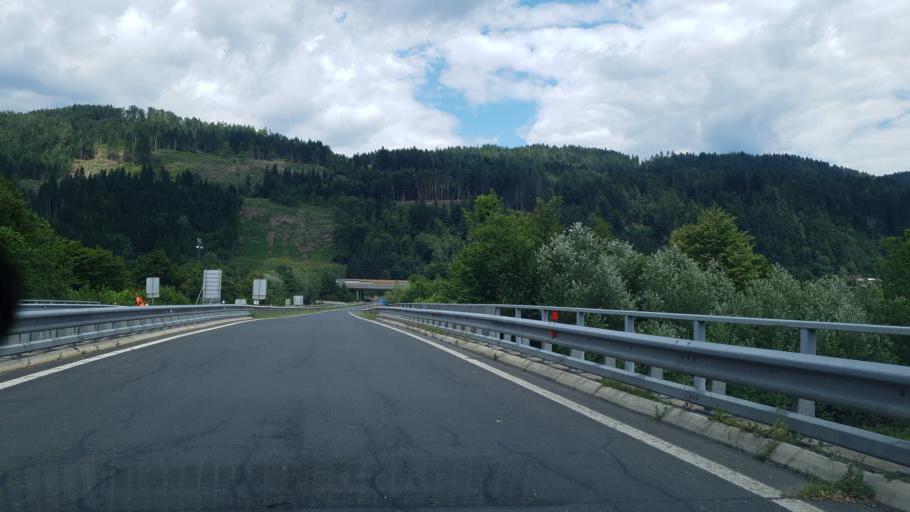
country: AT
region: Carinthia
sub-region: Politischer Bezirk Spittal an der Drau
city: Spittal an der Drau
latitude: 46.7790
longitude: 13.5383
